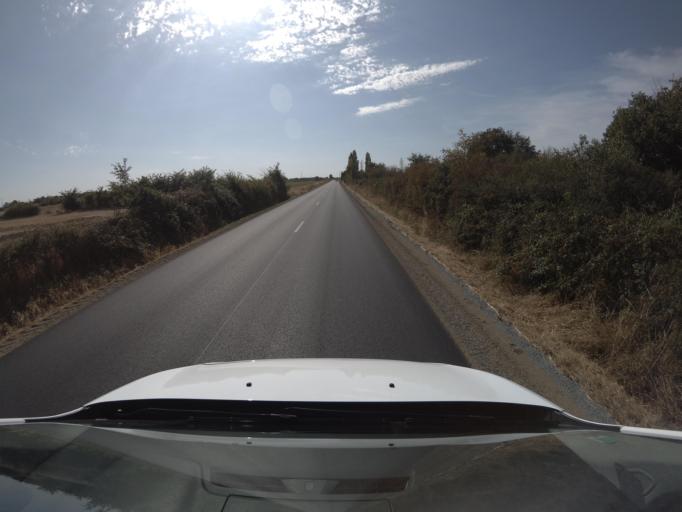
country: FR
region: Poitou-Charentes
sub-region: Departement des Deux-Sevres
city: Mauze-Thouarsais
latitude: 46.9989
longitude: -0.2972
